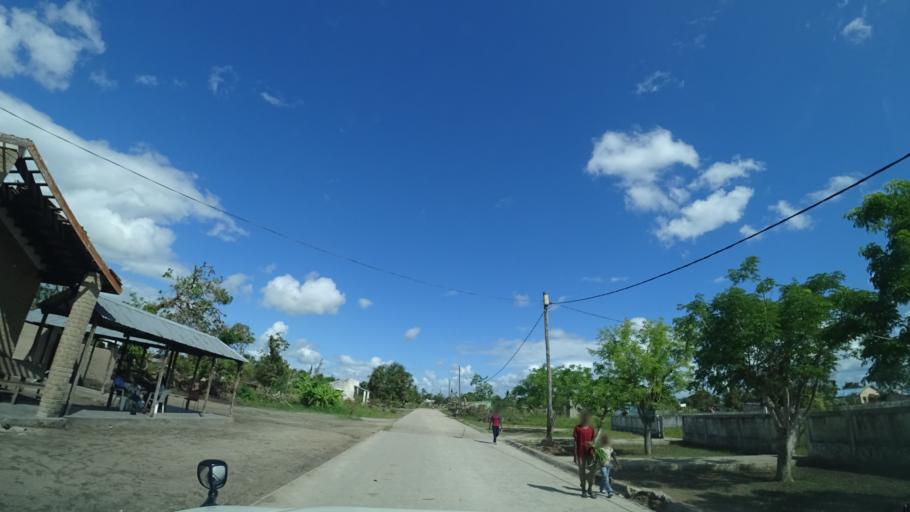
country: MZ
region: Sofala
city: Dondo
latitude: -19.4958
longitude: 34.5984
